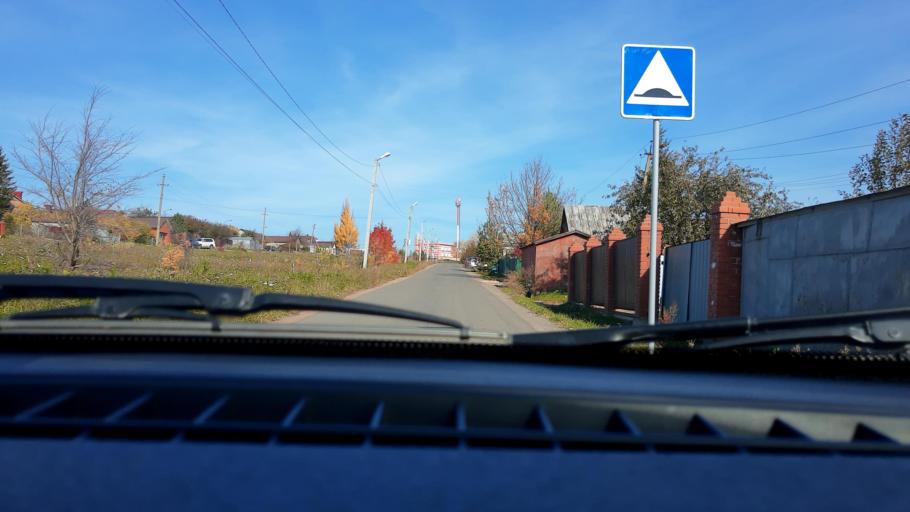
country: RU
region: Bashkortostan
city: Mikhaylovka
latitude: 54.8106
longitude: 55.8923
